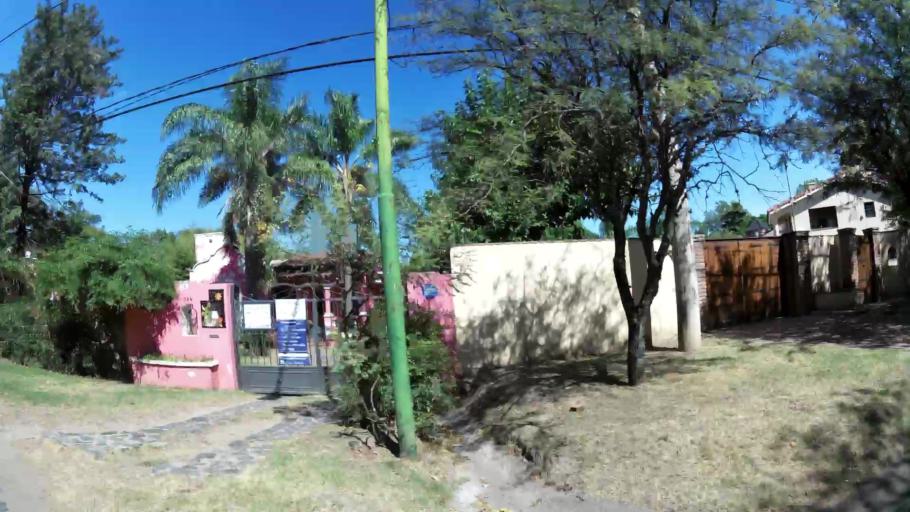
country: AR
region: Cordoba
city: Villa Allende
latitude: -31.2934
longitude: -64.2865
